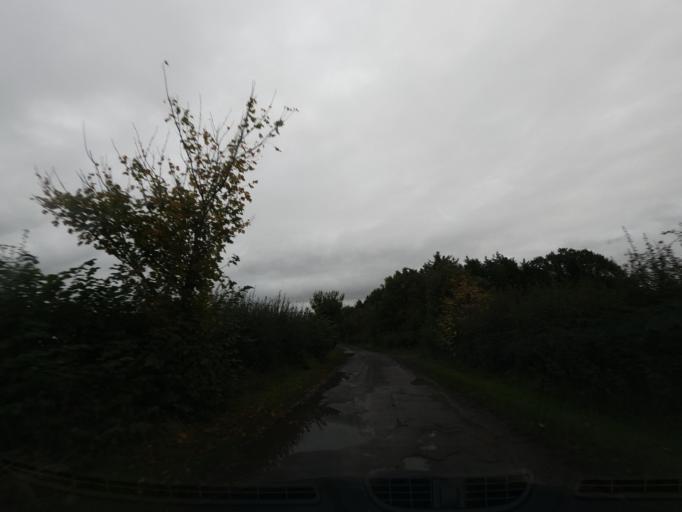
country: GB
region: England
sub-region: Northumberland
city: Ford
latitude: 55.6946
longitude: -2.0858
